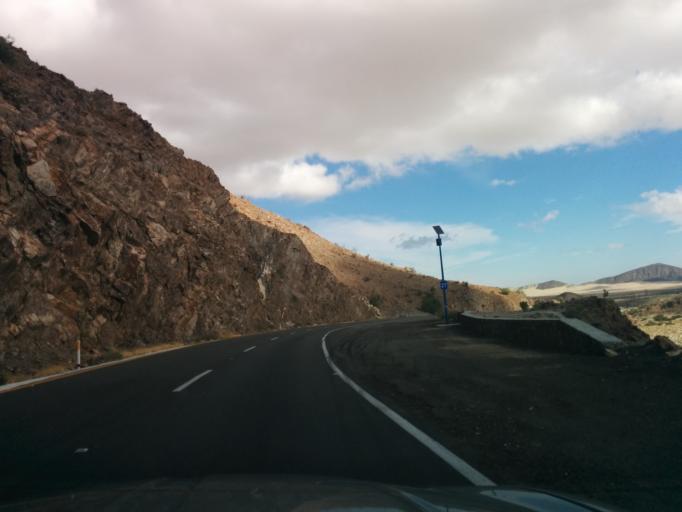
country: MX
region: Baja California
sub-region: Tecate
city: Cereso del Hongo
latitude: 32.5602
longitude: -115.9596
